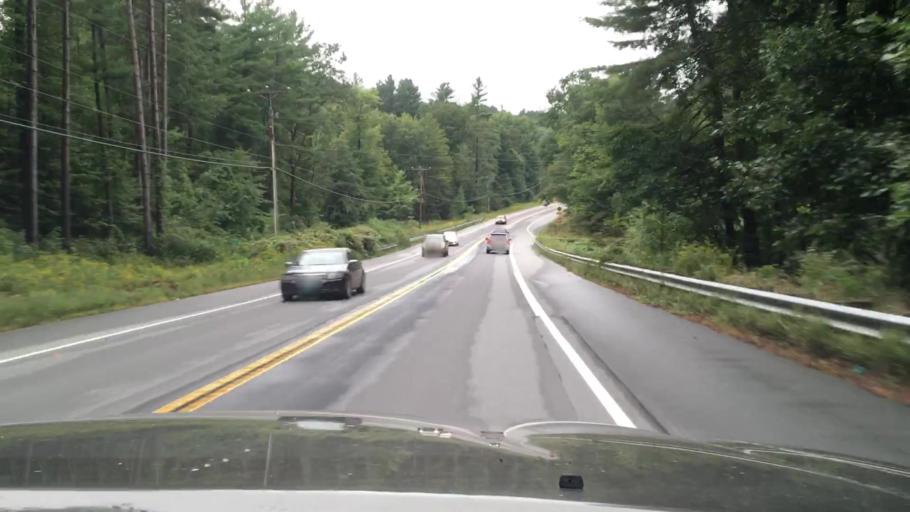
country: US
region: Vermont
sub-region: Windham County
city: Brattleboro
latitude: 42.8915
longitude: -72.5272
